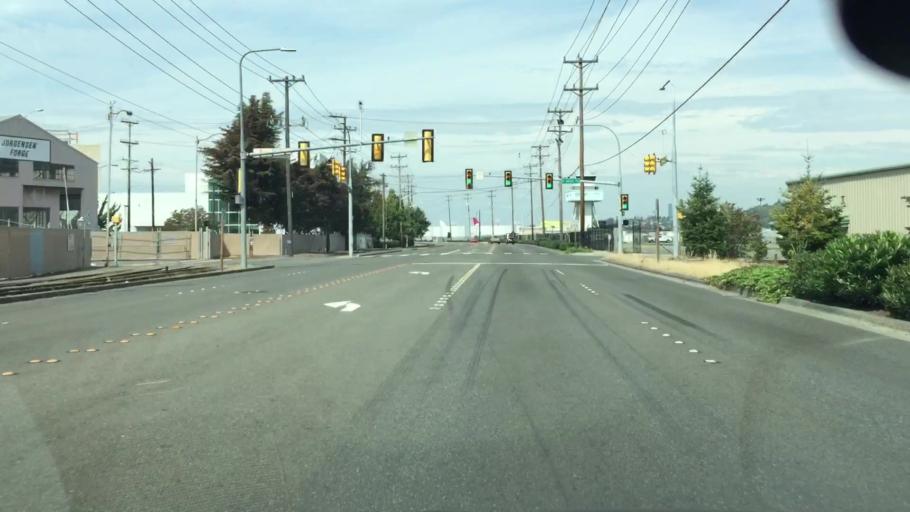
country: US
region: Washington
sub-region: King County
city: Boulevard Park
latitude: 47.5264
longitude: -122.3029
